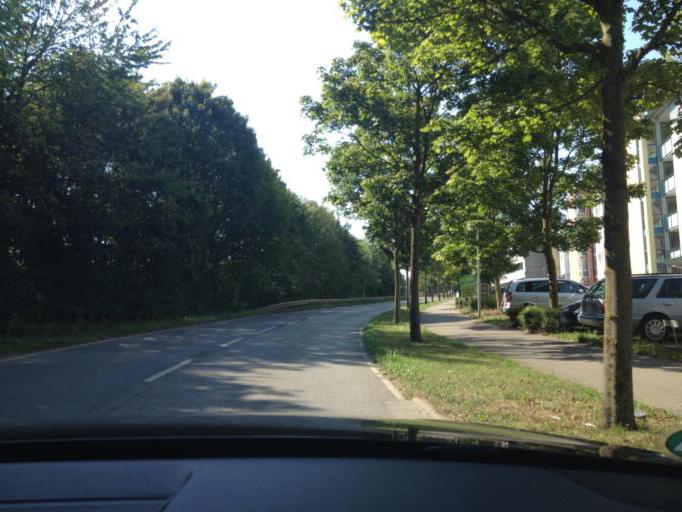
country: DE
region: Baden-Wuerttemberg
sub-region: Regierungsbezirk Stuttgart
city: Leinfelden-Echterdingen
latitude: 48.6936
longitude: 9.1745
